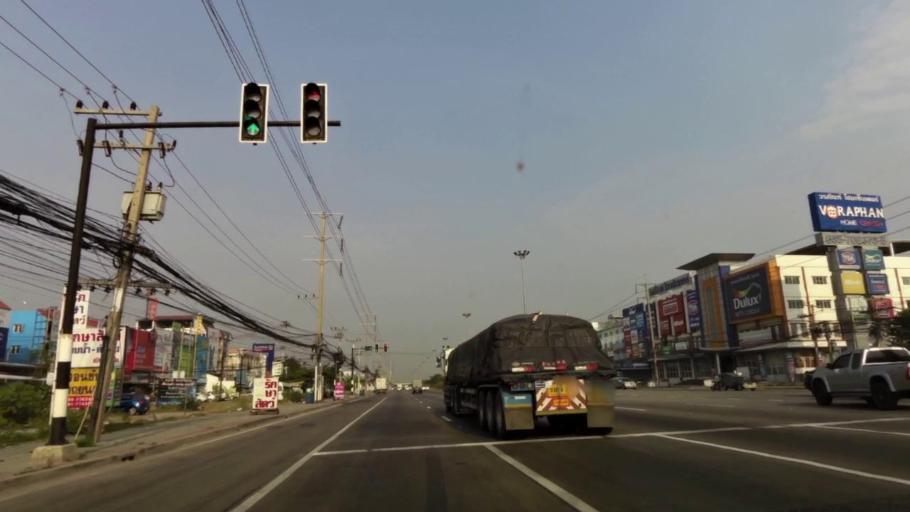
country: TH
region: Phra Nakhon Si Ayutthaya
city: Uthai
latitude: 14.3236
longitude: 100.6299
